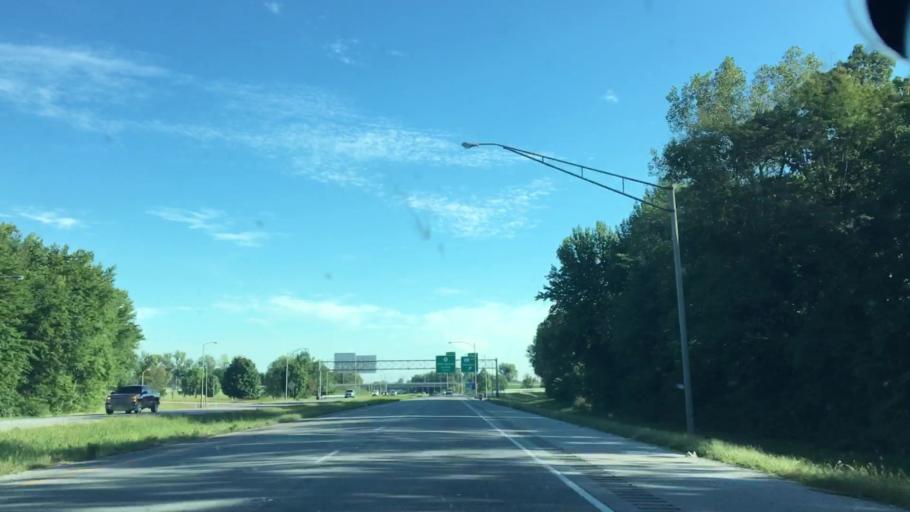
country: US
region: Kentucky
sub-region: Daviess County
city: Owensboro
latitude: 37.7711
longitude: -87.1653
